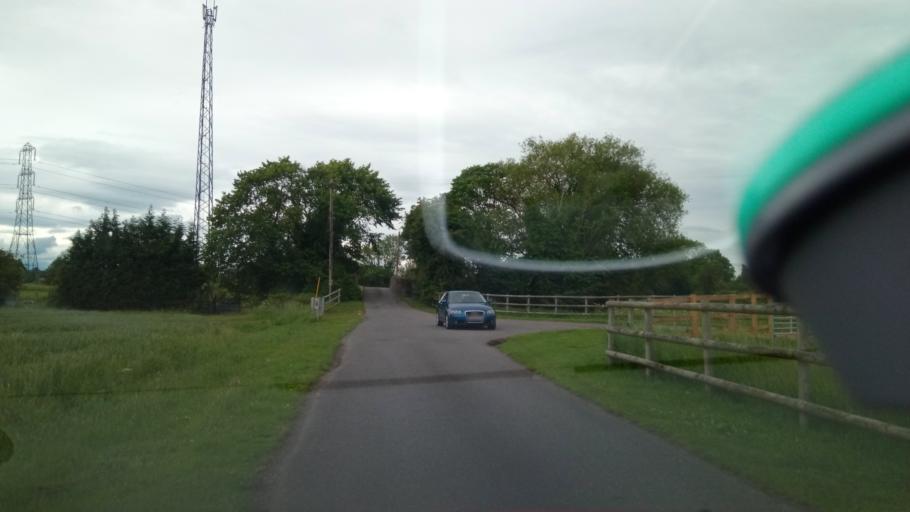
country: GB
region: England
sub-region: Derbyshire
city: Melbourne
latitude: 52.8476
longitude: -1.4161
